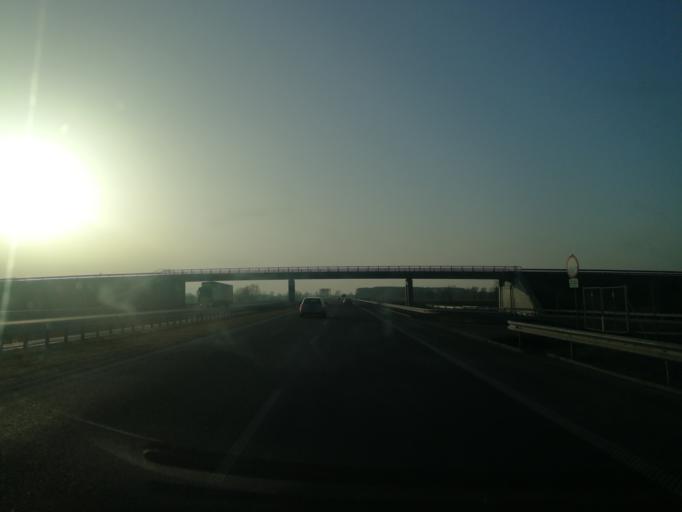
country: PL
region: Warmian-Masurian Voivodeship
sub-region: Powiat elblaski
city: Gronowo Elblaskie
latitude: 54.1644
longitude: 19.2710
